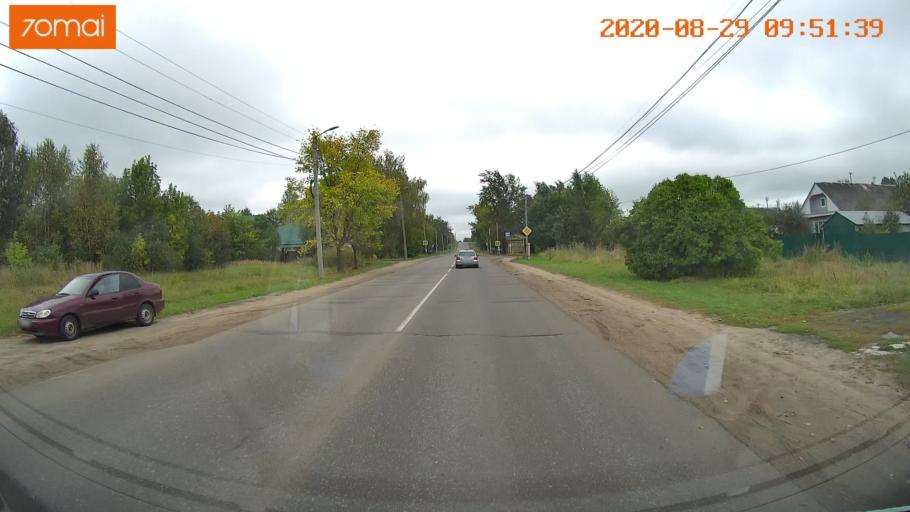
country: RU
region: Ivanovo
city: Kineshma
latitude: 57.4285
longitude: 42.2004
